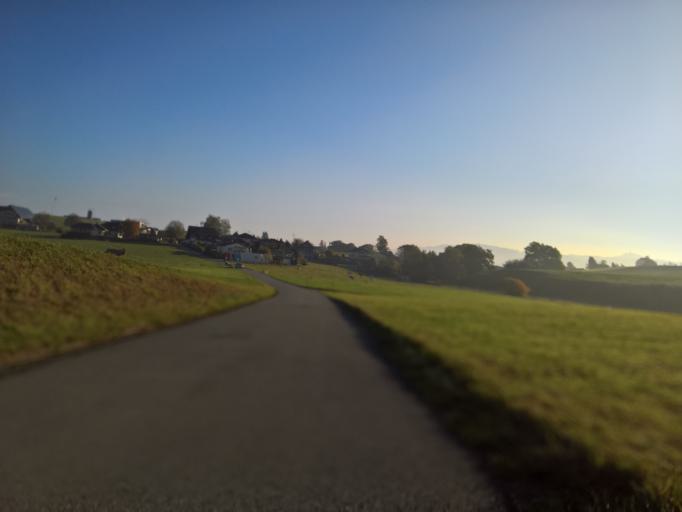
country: CH
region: Bern
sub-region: Bern-Mittelland District
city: Kirchlindach
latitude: 46.9960
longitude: 7.4295
